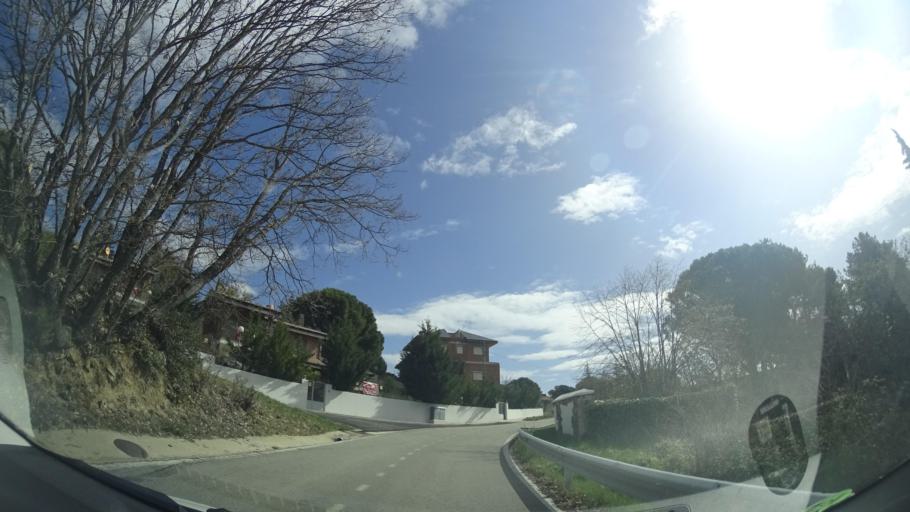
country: ES
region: Madrid
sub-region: Provincia de Madrid
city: Miraflores de la Sierra
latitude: 40.8203
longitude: -3.7615
